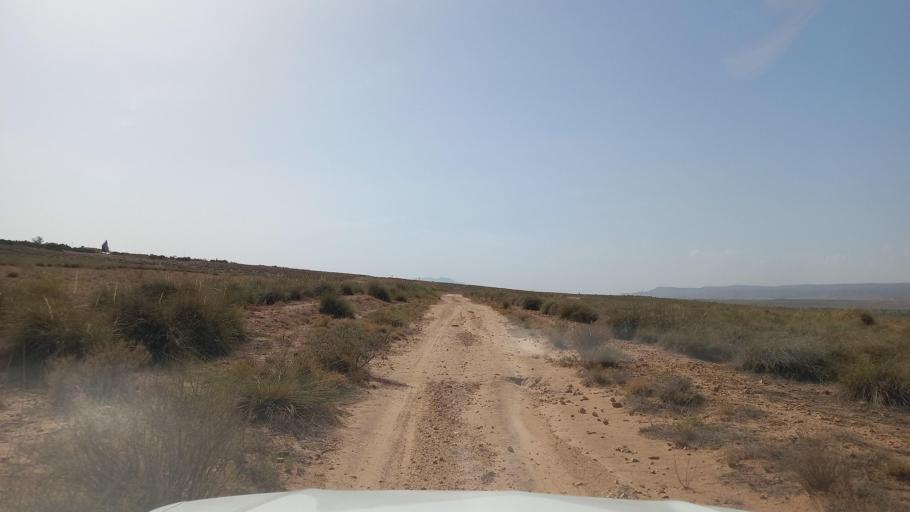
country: TN
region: Al Qasrayn
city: Kasserine
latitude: 35.2145
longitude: 8.9920
